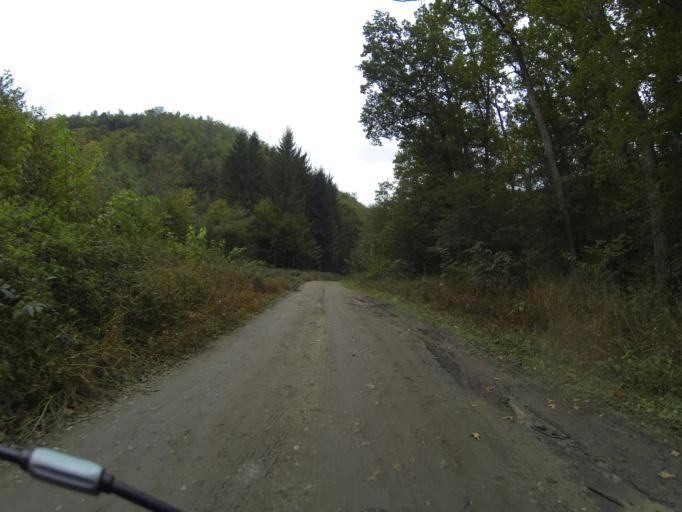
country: RO
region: Gorj
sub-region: Comuna Tismana
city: Pocruia
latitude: 45.0564
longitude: 22.9057
